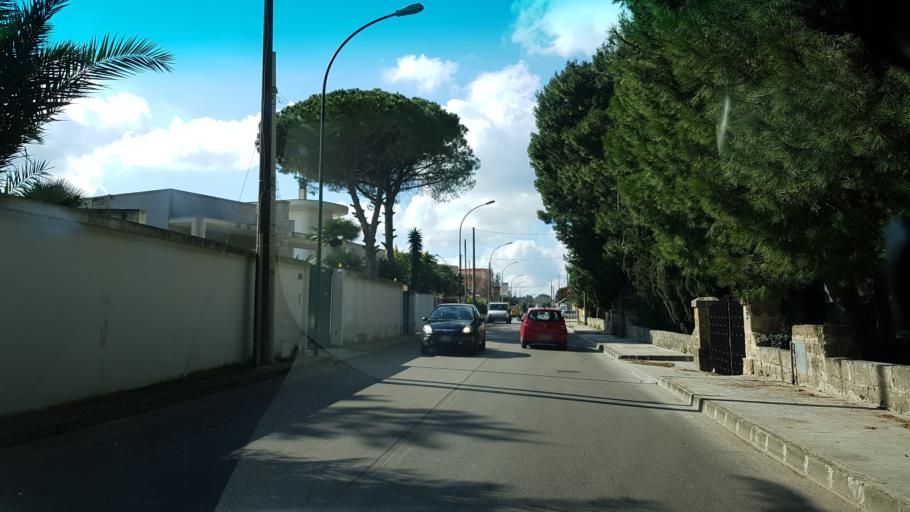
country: IT
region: Apulia
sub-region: Provincia di Lecce
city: Squinzano
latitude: 40.4300
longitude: 18.0373
